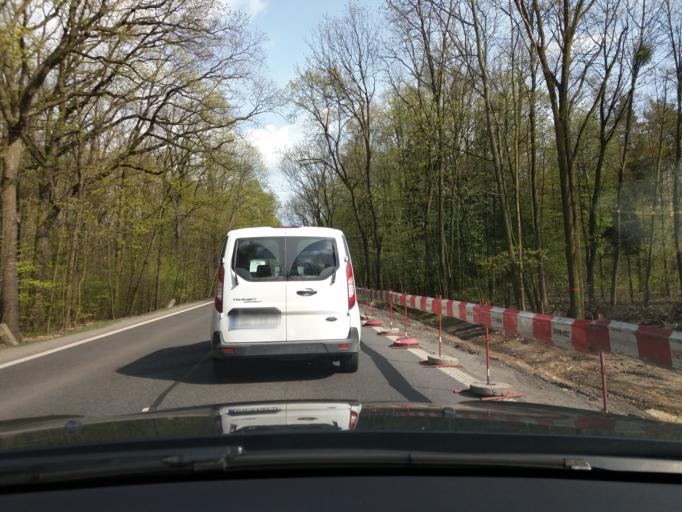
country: PL
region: Lower Silesian Voivodeship
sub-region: Powiat sredzki
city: Mrozow
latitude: 51.1486
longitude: 16.8434
